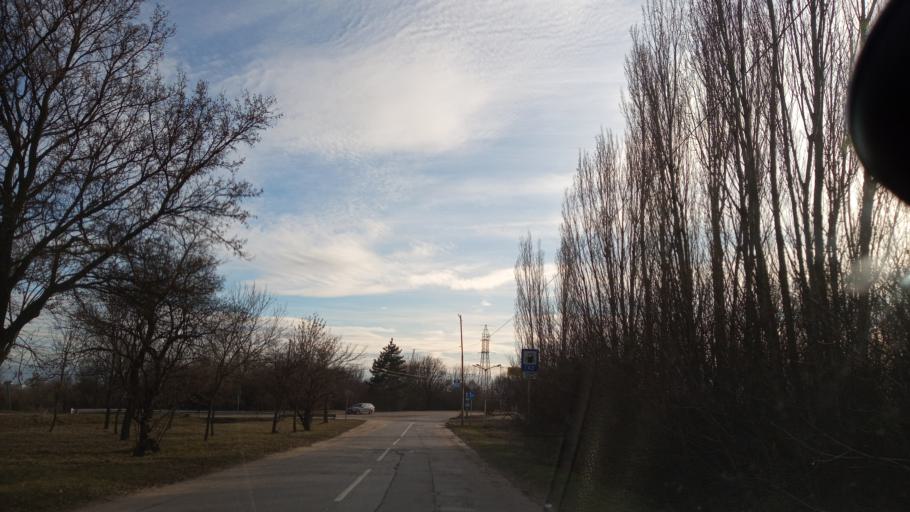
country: BG
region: Sofia-Capital
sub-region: Stolichna Obshtina
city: Bukhovo
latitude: 42.7562
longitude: 23.5597
